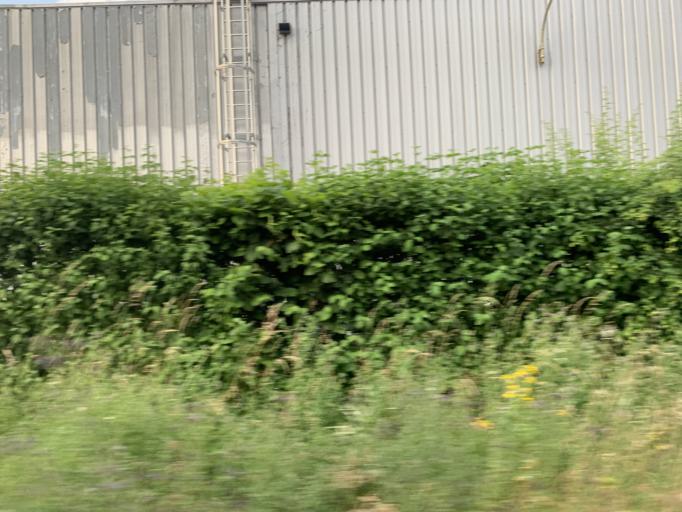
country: FR
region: Rhone-Alpes
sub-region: Departement du Rhone
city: Meyzieu
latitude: 45.7679
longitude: 5.0292
